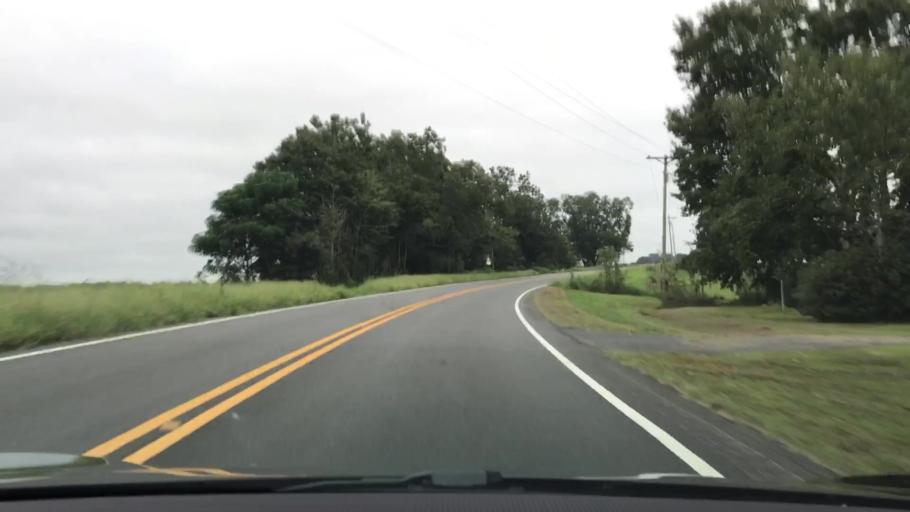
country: US
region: Alabama
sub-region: Covington County
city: Opp
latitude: 31.2651
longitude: -86.1625
